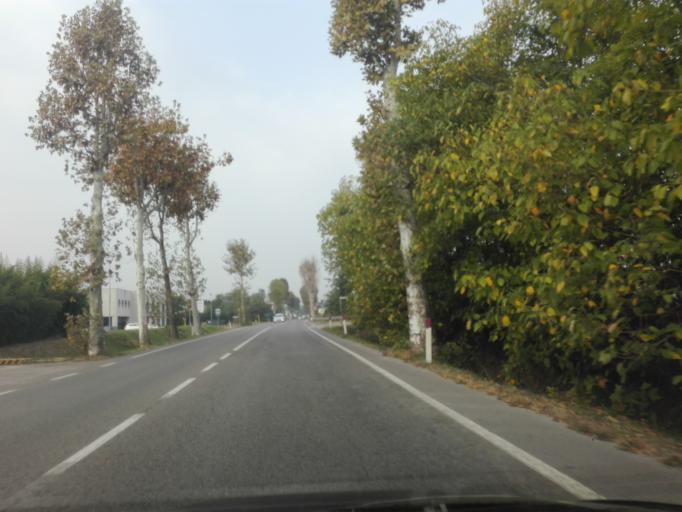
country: IT
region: Veneto
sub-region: Provincia di Verona
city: Sona
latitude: 45.4458
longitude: 10.8448
